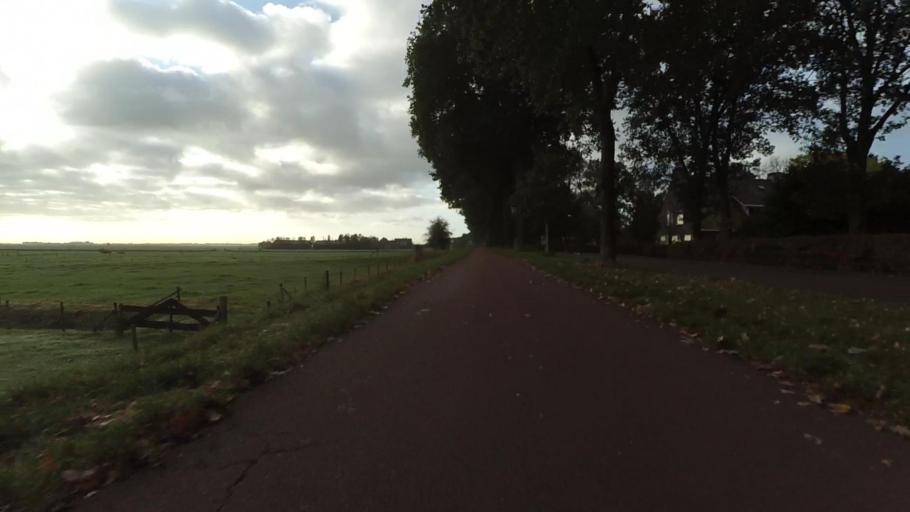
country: NL
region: North Holland
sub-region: Gemeente Blaricum
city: Blaricum
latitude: 52.2600
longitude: 5.2702
